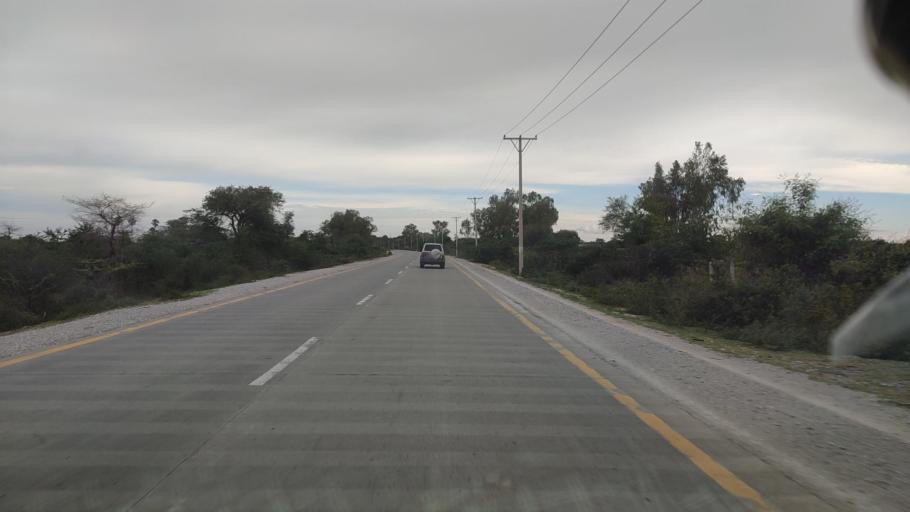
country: MM
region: Mandalay
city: Meiktila
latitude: 21.1878
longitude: 96.0240
